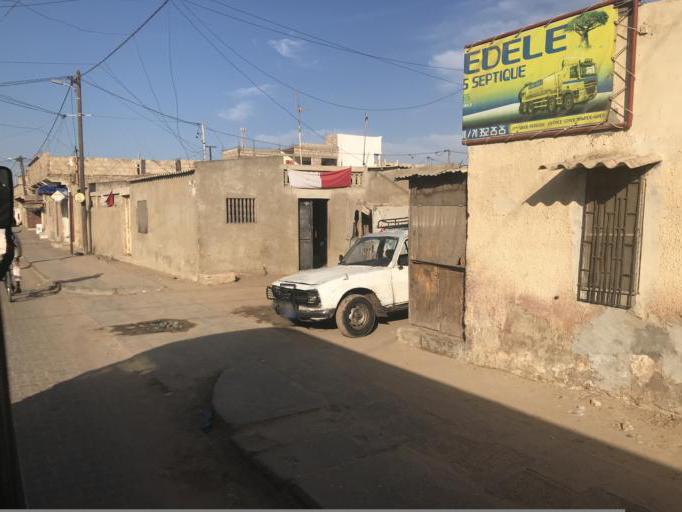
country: SN
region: Saint-Louis
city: Saint-Louis
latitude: 16.0075
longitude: -16.4946
